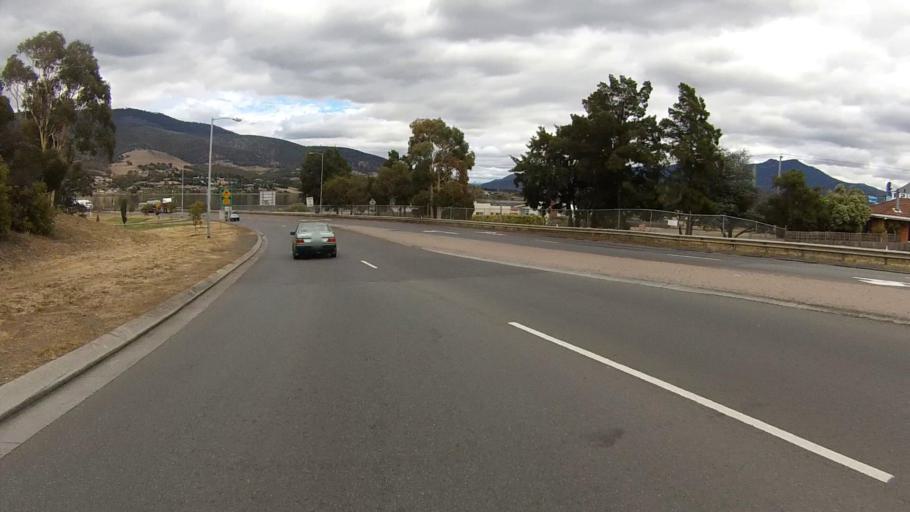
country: AU
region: Tasmania
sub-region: Brighton
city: Bridgewater
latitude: -42.7383
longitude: 147.2274
